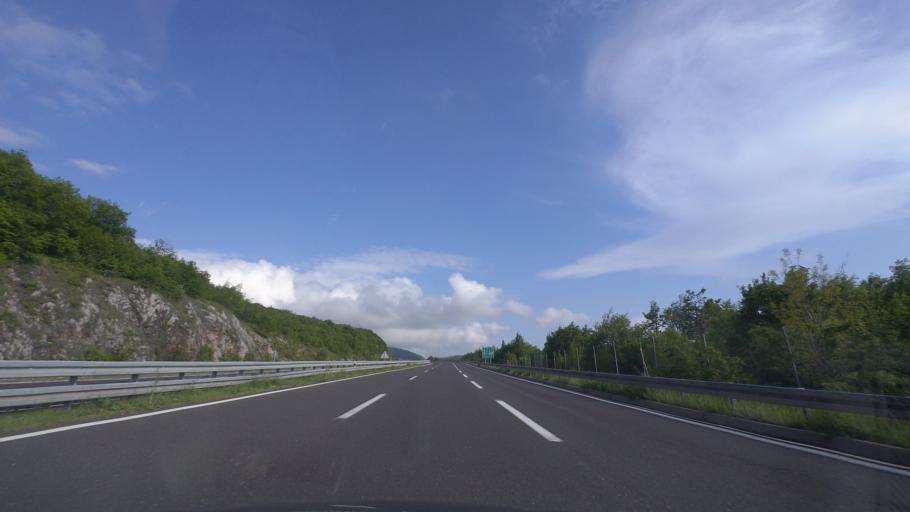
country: HR
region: Primorsko-Goranska
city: Krasica
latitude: 45.3582
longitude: 14.5772
